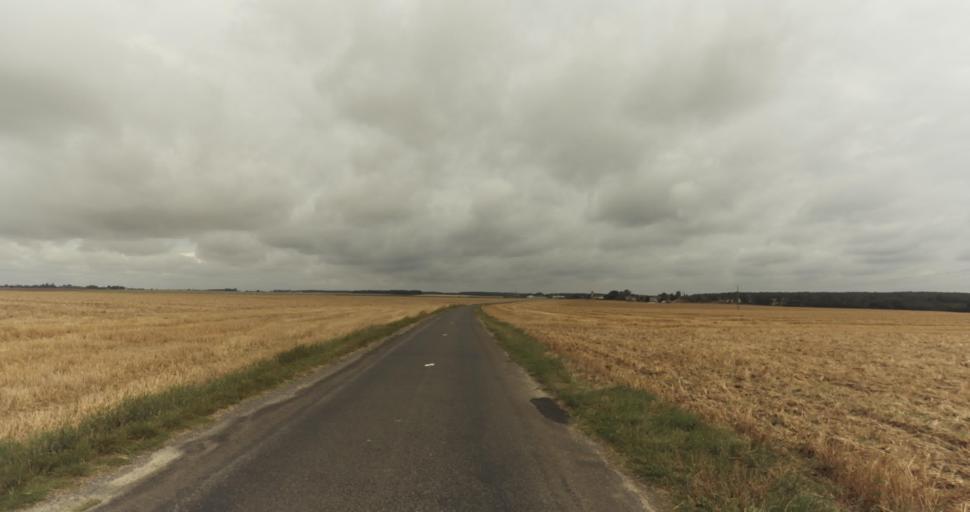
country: FR
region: Haute-Normandie
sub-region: Departement de l'Eure
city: La Couture-Boussey
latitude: 48.9228
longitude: 1.4012
